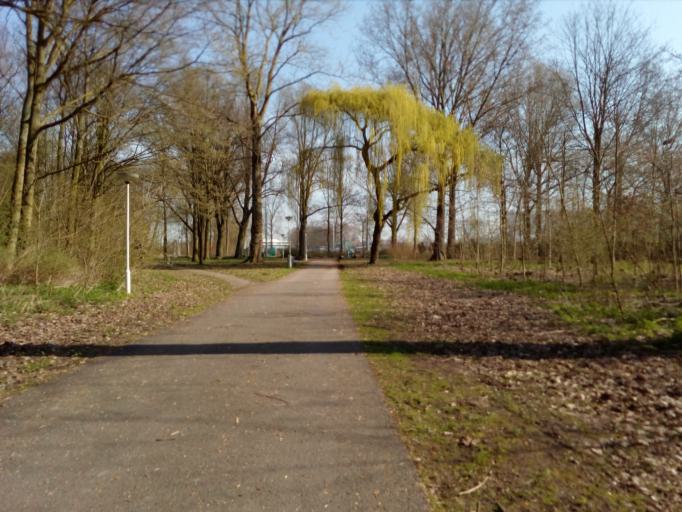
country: NL
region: South Holland
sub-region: Gemeente Zoetermeer
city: Zoetermeer
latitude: 52.0465
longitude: 4.5228
